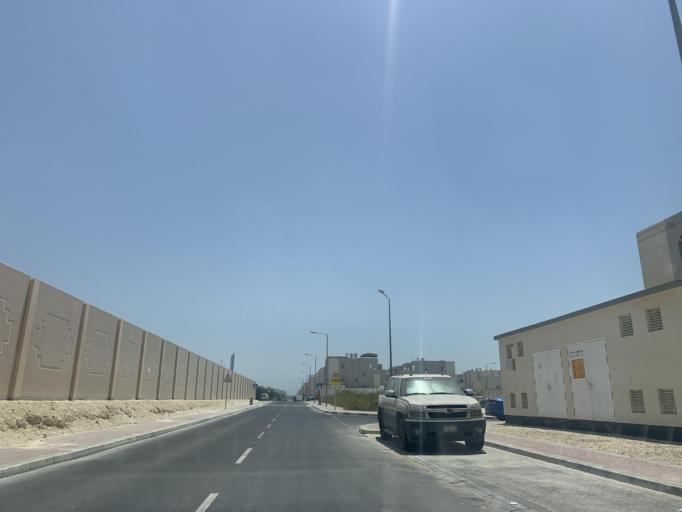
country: BH
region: Manama
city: Jidd Hafs
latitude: 26.2344
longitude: 50.4634
